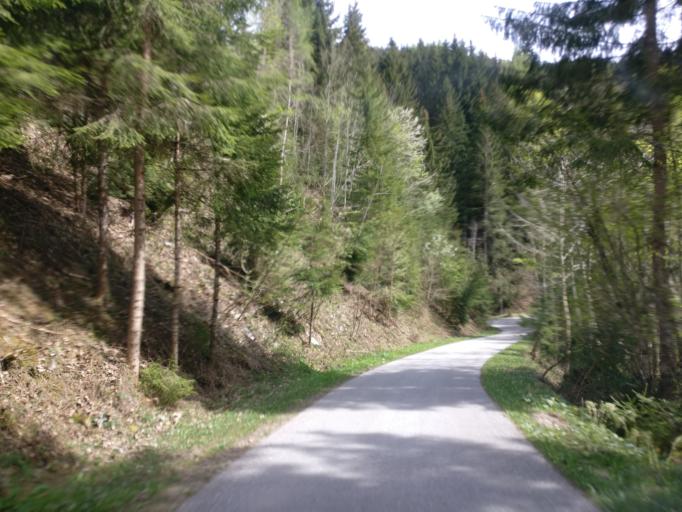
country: AT
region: Salzburg
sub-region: Politischer Bezirk Sankt Johann im Pongau
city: Pfarrwerfen
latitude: 47.4820
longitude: 13.2097
